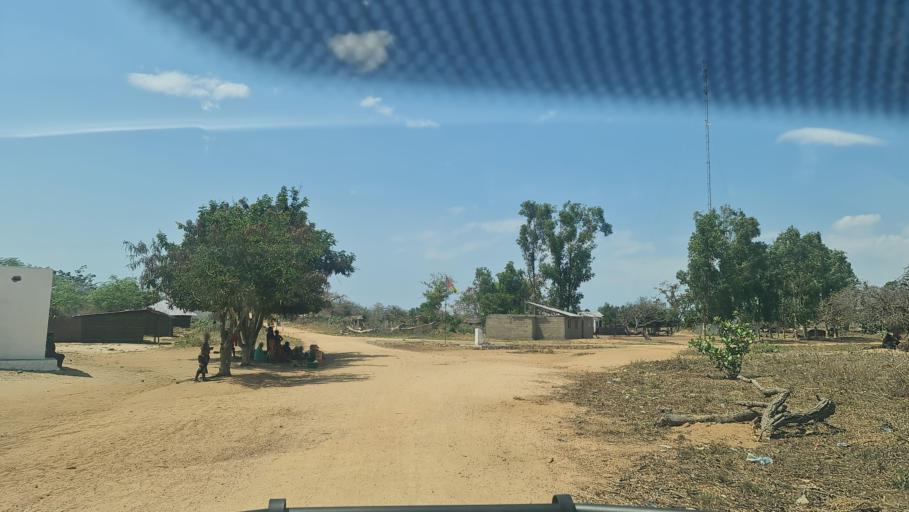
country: MZ
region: Nampula
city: Ilha de Mocambique
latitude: -15.1955
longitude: 40.5250
